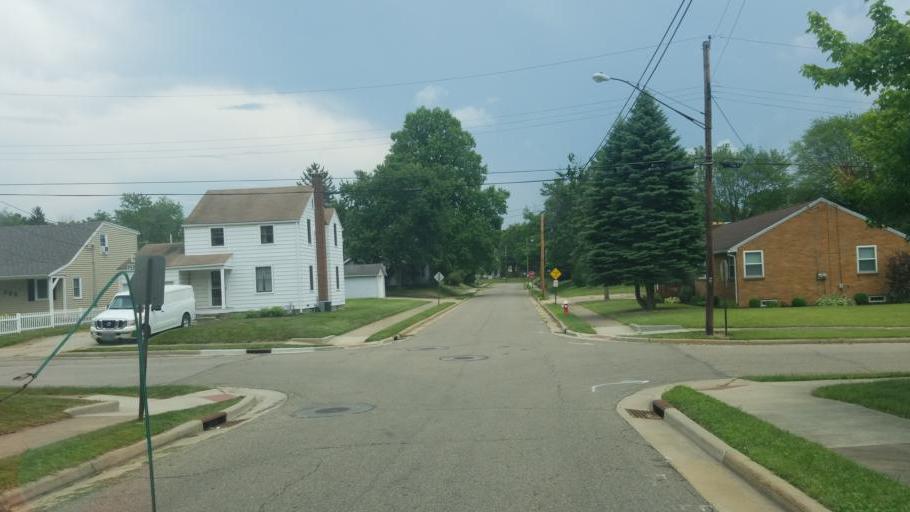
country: US
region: Ohio
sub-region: Stark County
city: North Canton
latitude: 40.8783
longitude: -81.3953
